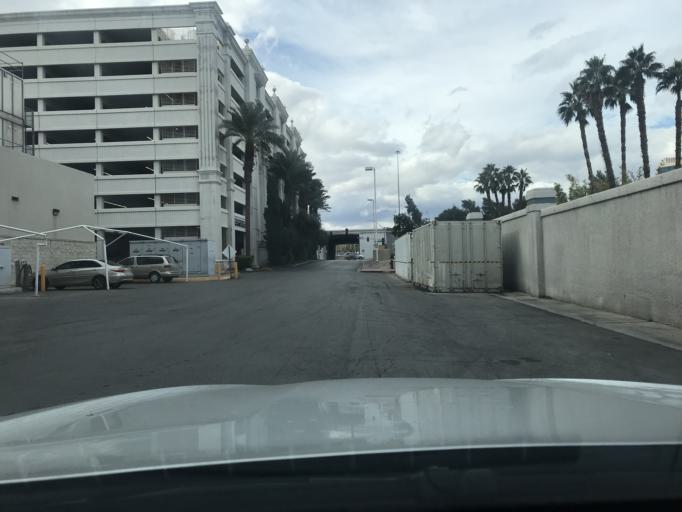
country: US
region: Nevada
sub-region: Clark County
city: Paradise
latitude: 36.1198
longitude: -115.1783
